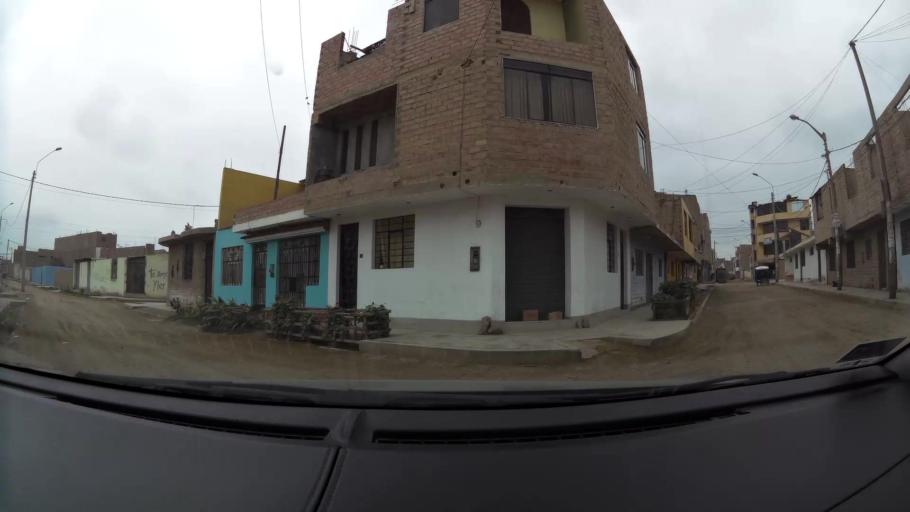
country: PE
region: Lima
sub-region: Provincia de Huaral
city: Huaral
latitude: -11.5015
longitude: -77.2122
